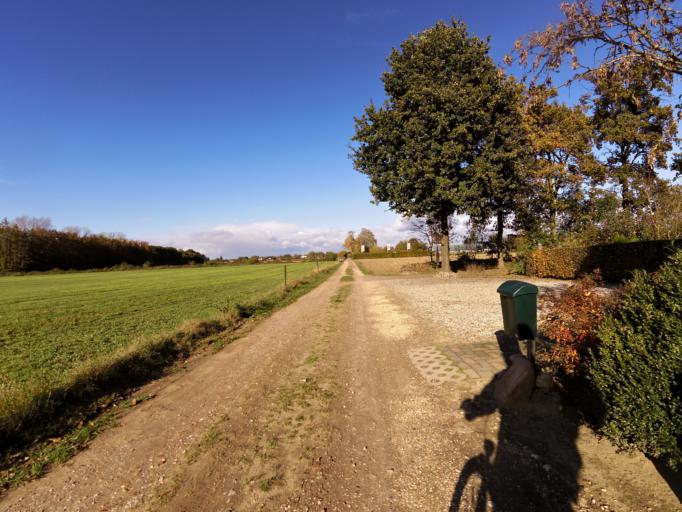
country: NL
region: Gelderland
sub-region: Gemeente Doetinchem
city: Doetinchem
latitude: 51.9470
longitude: 6.2129
